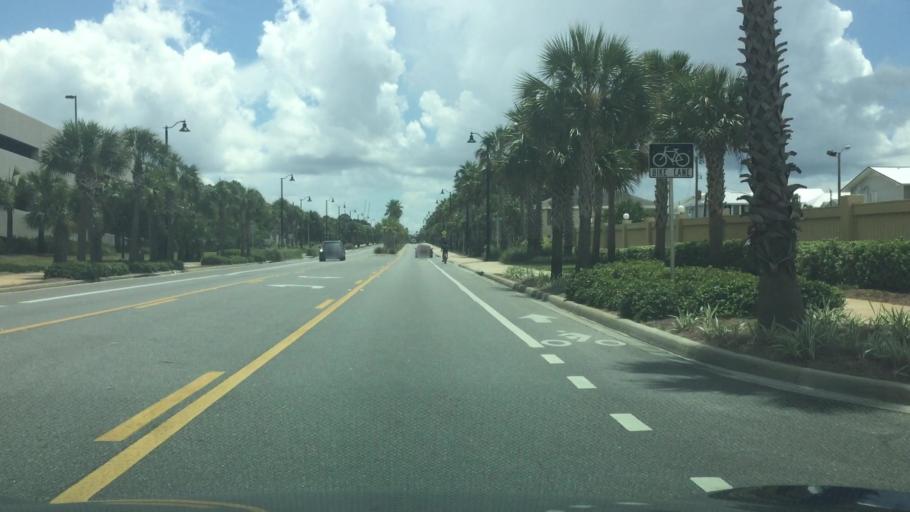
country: US
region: Florida
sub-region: Bay County
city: Panama City Beach
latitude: 30.1754
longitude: -85.8036
